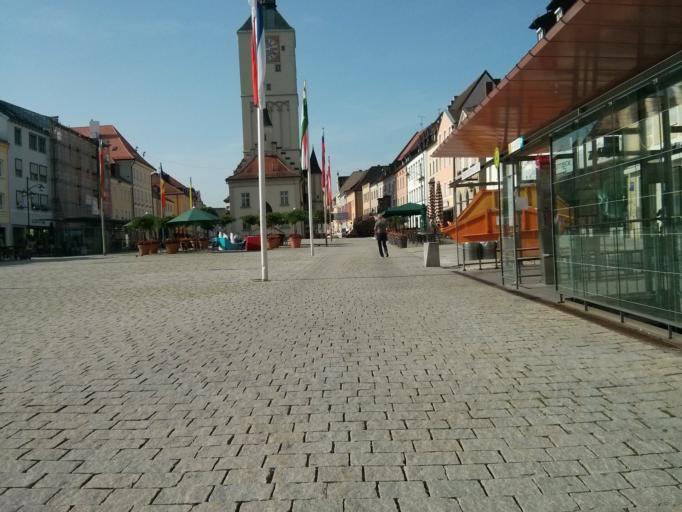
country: DE
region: Bavaria
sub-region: Lower Bavaria
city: Deggendorf
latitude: 48.8349
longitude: 12.9621
